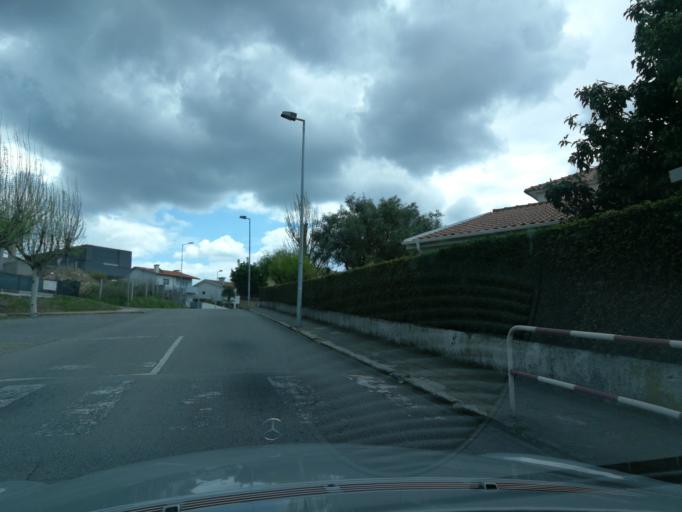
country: PT
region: Braga
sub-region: Braga
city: Braga
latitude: 41.5333
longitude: -8.4144
